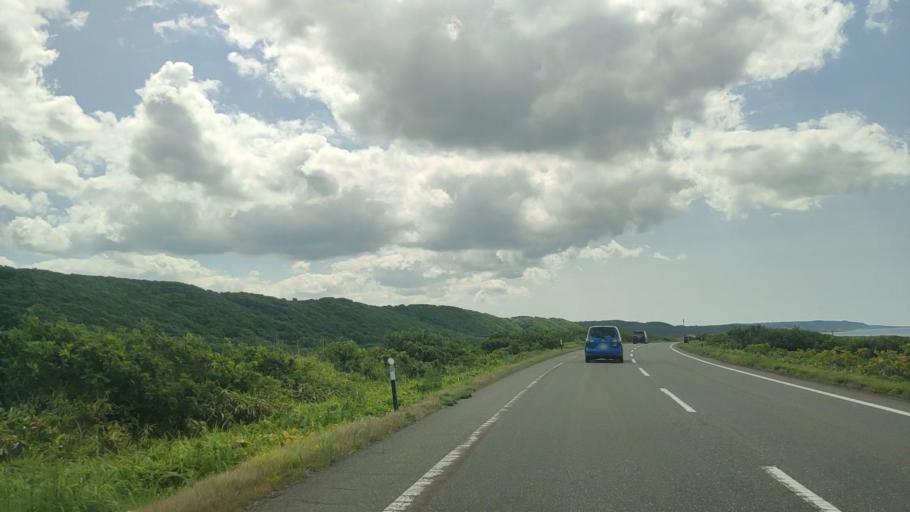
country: JP
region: Hokkaido
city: Wakkanai
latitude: 45.2969
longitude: 141.6238
